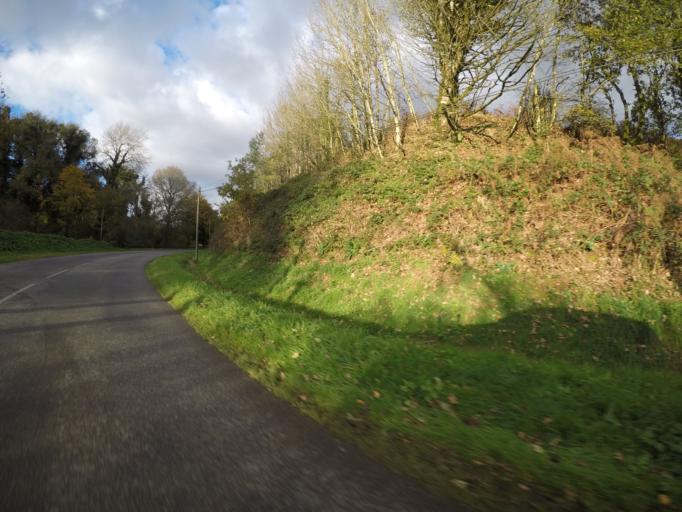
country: FR
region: Brittany
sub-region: Departement des Cotes-d'Armor
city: Callac
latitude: 48.4329
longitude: -3.3297
